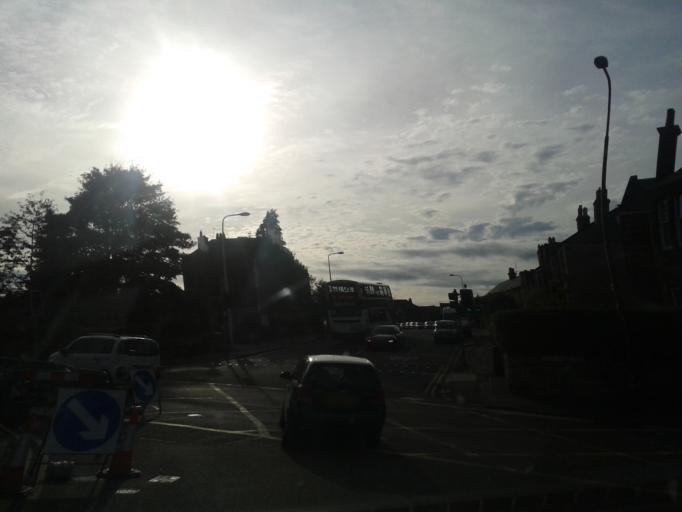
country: GB
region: Scotland
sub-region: Edinburgh
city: Edinburgh
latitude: 55.9193
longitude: -3.2125
